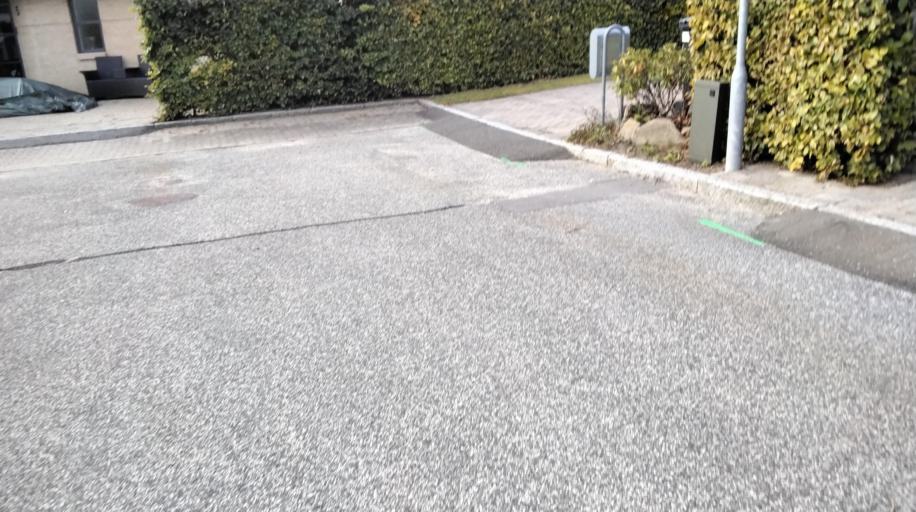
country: DK
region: Zealand
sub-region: Naestved Kommune
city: Naestved
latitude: 55.2254
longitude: 11.7290
